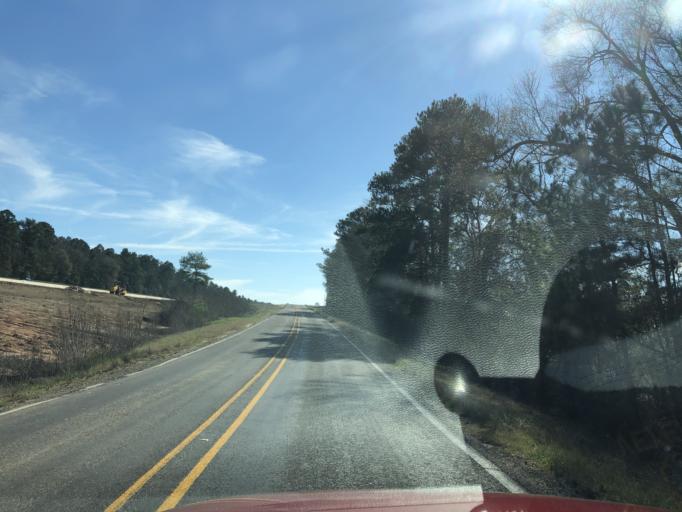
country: US
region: Texas
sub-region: Walker County
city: New Waverly
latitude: 30.6212
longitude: -95.5080
